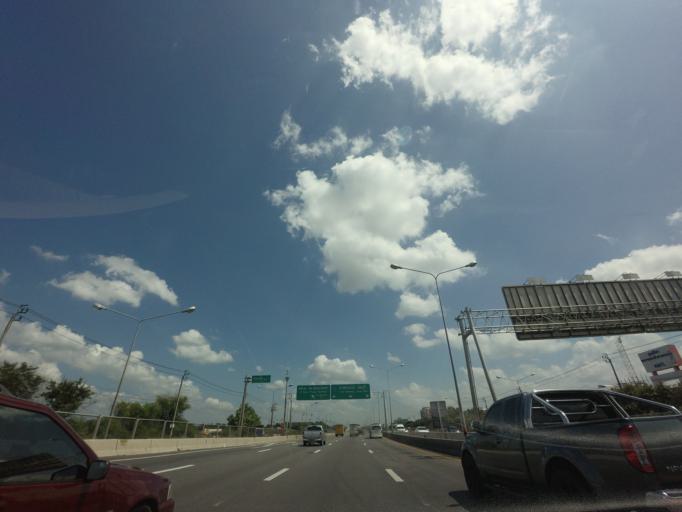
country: TH
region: Bangkok
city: Lat Krabang
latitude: 13.7321
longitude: 100.7716
